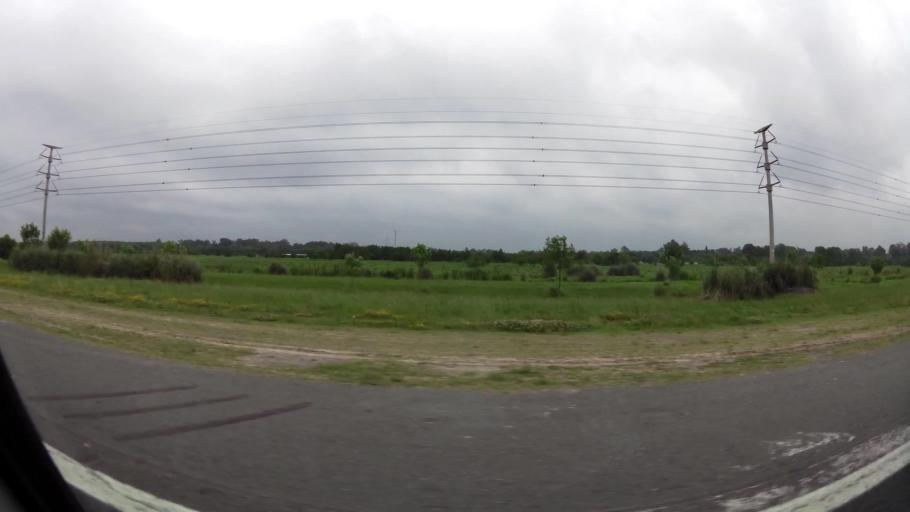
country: AR
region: Buenos Aires
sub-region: Partido de La Plata
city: La Plata
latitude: -34.8323
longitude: -58.0868
